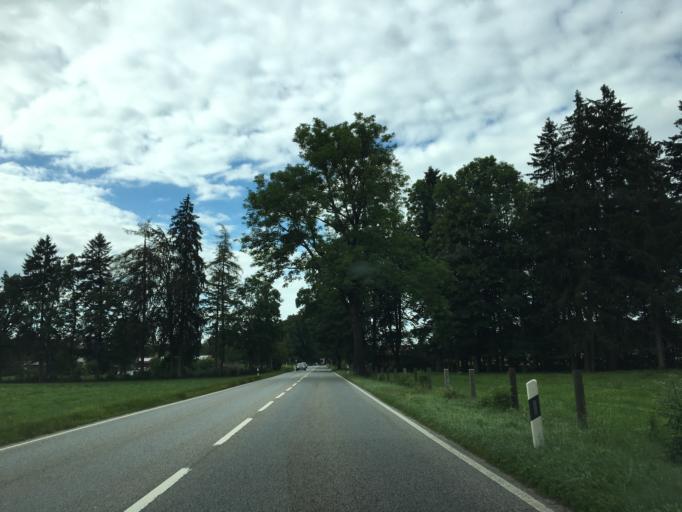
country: DE
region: Bavaria
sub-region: Upper Bavaria
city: Warngau
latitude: 47.7924
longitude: 11.7207
